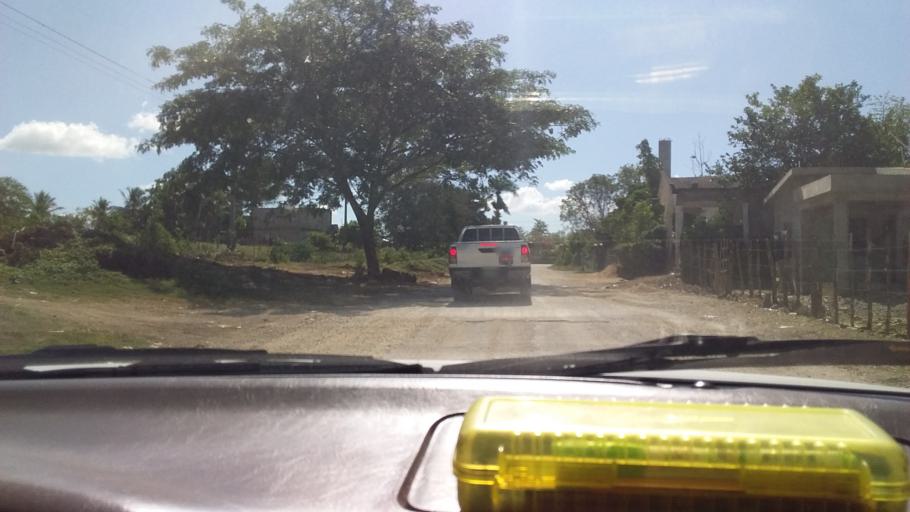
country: DO
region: Santo Domingo
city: Guerra
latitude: 18.5634
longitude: -69.7785
